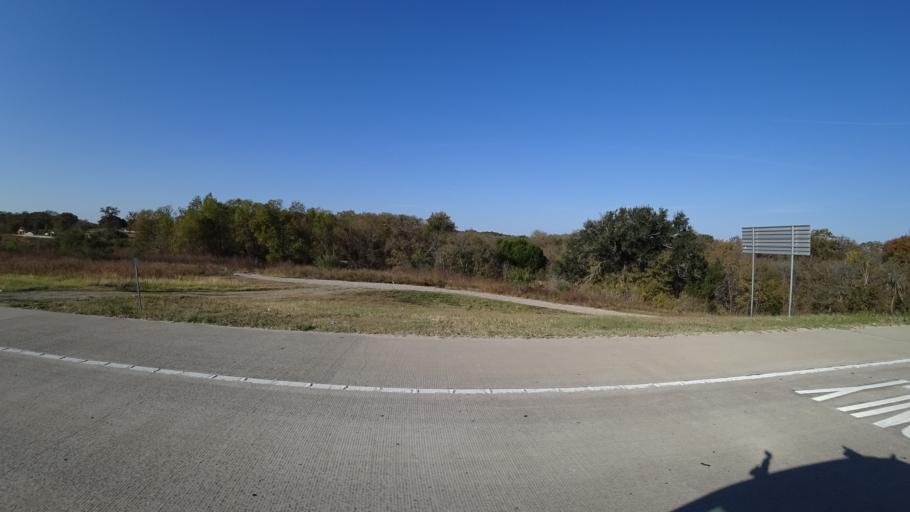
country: US
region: Texas
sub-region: Williamson County
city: Hutto
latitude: 30.5232
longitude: -97.5761
